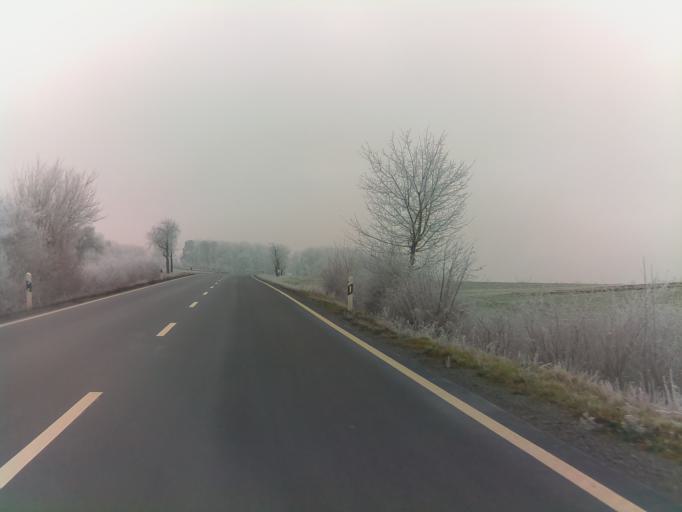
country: DE
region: Baden-Wuerttemberg
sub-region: Regierungsbezirk Stuttgart
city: Boxberg
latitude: 49.4677
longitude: 9.6172
